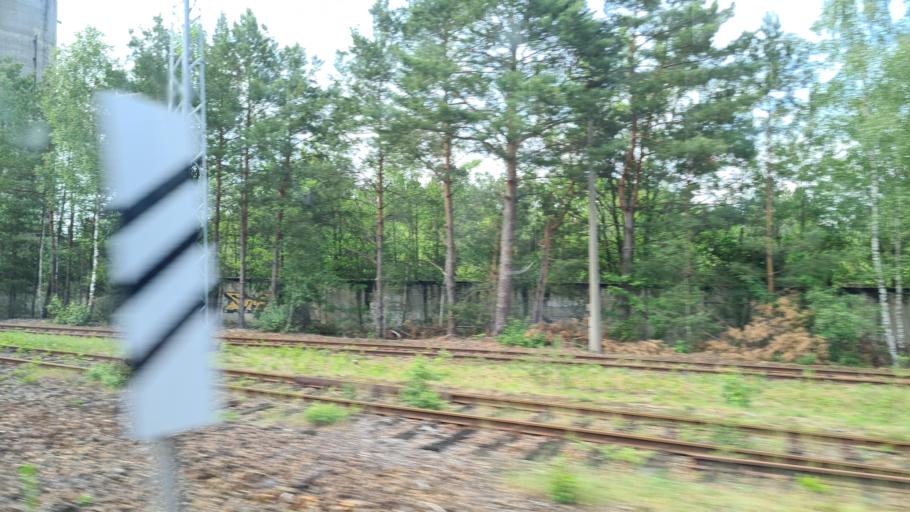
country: DE
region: Brandenburg
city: Schonewalde
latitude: 51.6290
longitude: 13.6301
